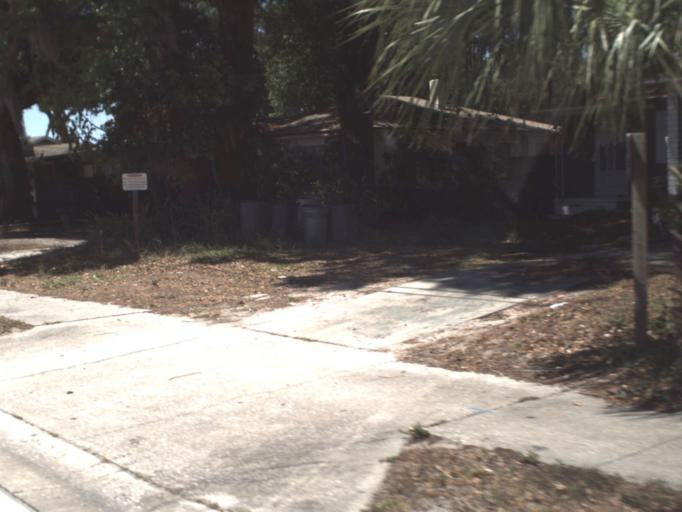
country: US
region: Florida
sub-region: Orange County
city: Fairview Shores
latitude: 28.5966
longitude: -81.3906
